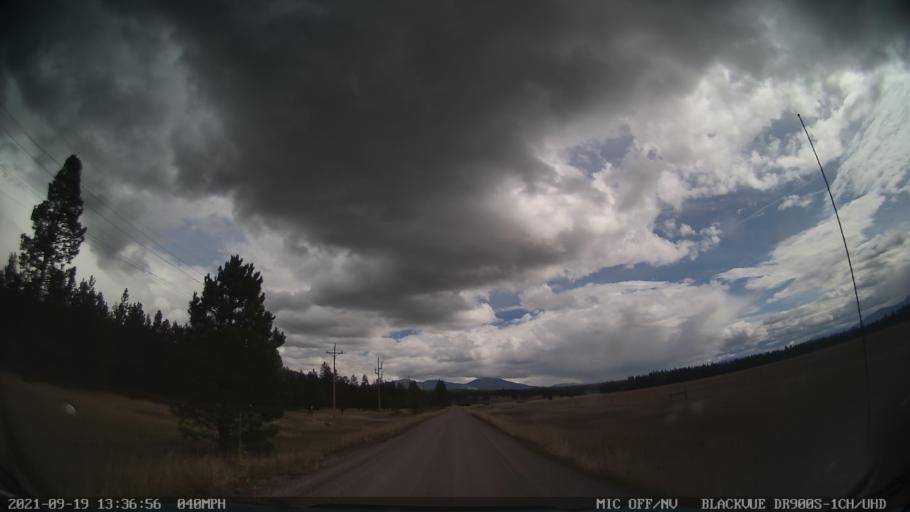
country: US
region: Montana
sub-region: Missoula County
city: Seeley Lake
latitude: 47.1066
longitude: -113.2910
